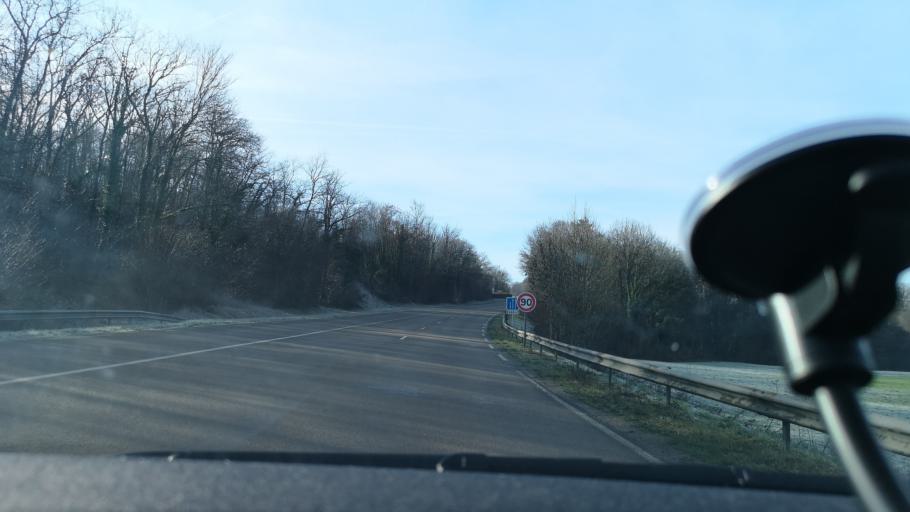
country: FR
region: Franche-Comte
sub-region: Departement du Doubs
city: Roulans
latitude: 47.3308
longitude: 6.2695
